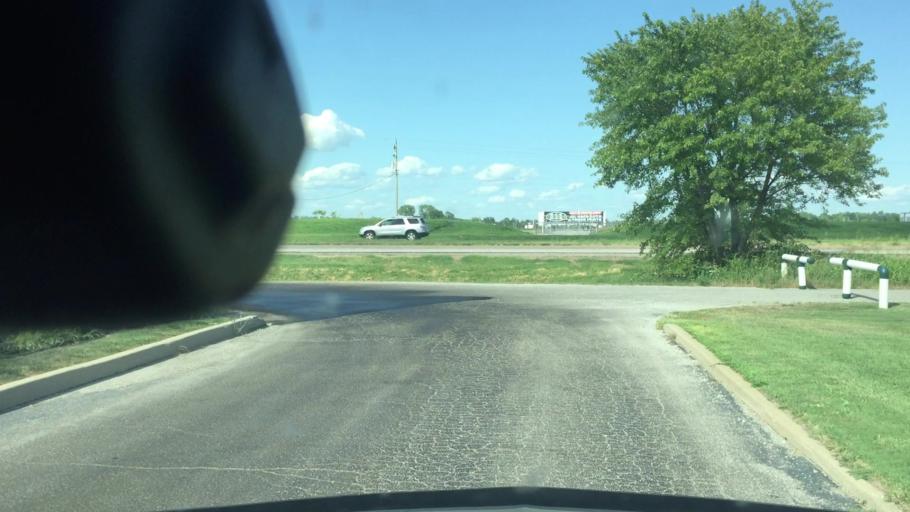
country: US
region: Illinois
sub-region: Madison County
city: Madison
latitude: 38.6602
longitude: -90.1388
